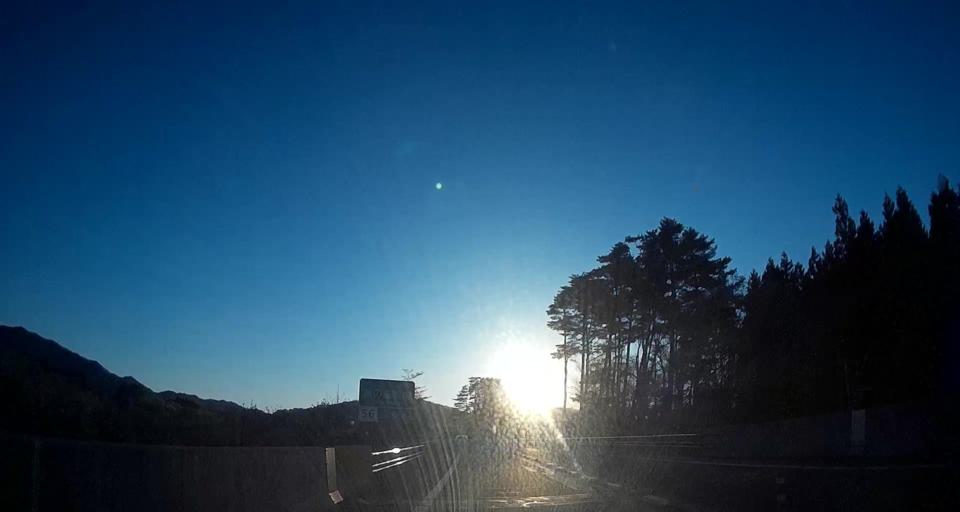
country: JP
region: Iwate
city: Miyako
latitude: 39.8764
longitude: 141.9336
